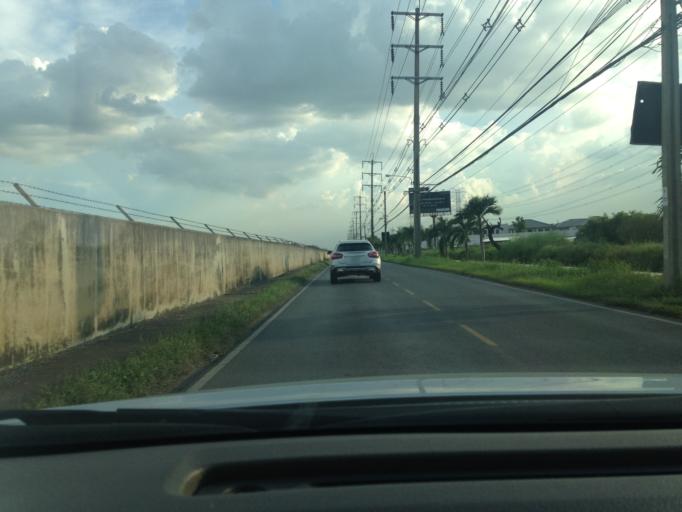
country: TH
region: Bangkok
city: Don Mueang
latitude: 13.9290
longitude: 100.5622
